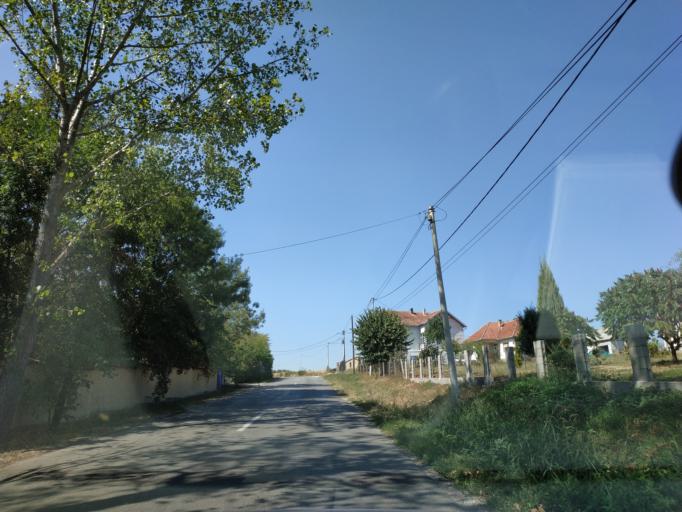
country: RS
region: Central Serbia
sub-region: Sumadijski Okrug
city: Topola
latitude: 44.2659
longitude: 20.6693
